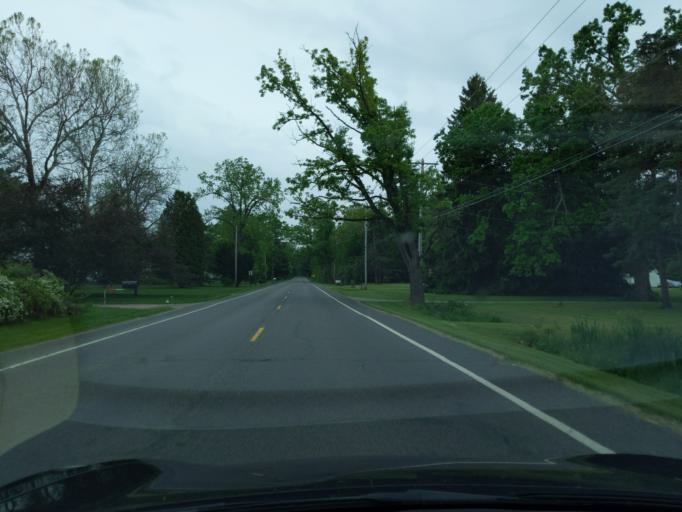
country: US
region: Michigan
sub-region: Ingham County
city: Haslett
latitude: 42.7269
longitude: -84.3635
